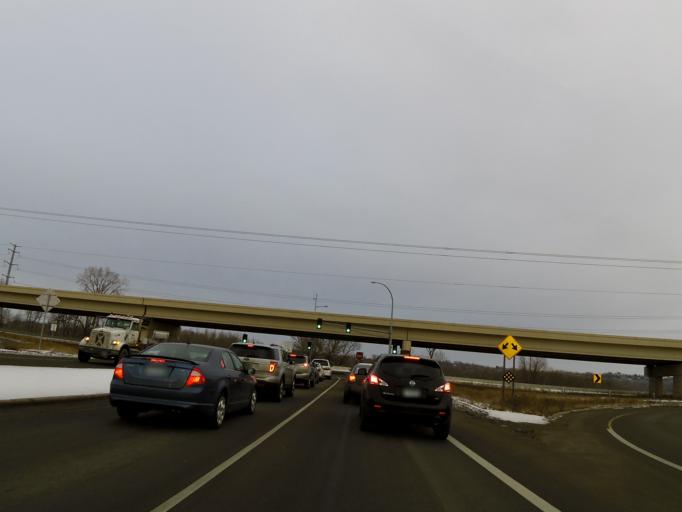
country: US
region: Minnesota
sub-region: Scott County
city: Savage
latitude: 44.7783
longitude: -93.3781
